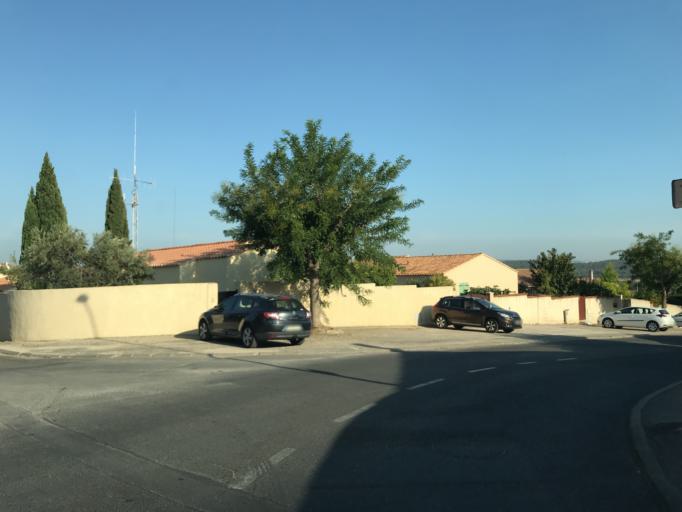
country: FR
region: Provence-Alpes-Cote d'Azur
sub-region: Departement des Bouches-du-Rhone
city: La Fare-les-Oliviers
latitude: 43.5550
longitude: 5.2004
